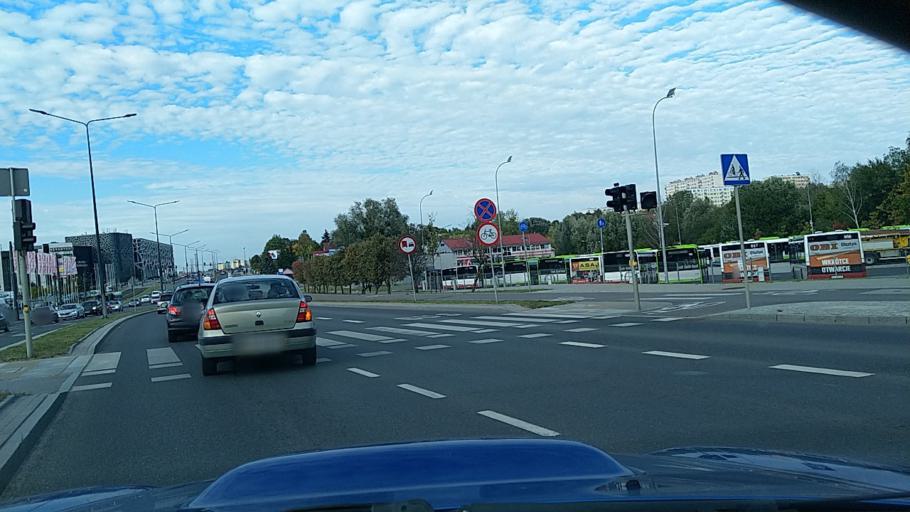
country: PL
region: Warmian-Masurian Voivodeship
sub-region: Powiat olsztynski
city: Olsztyn
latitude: 53.7499
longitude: 20.4865
